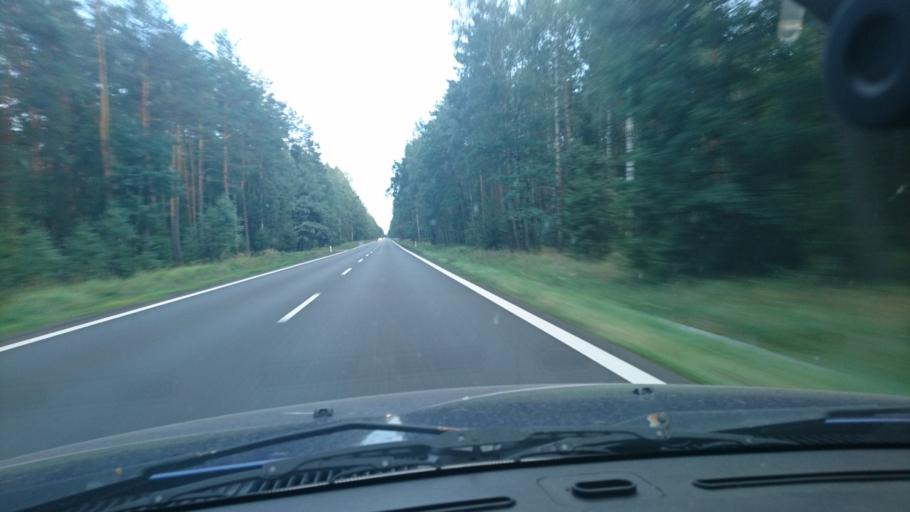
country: PL
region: Silesian Voivodeship
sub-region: Powiat tarnogorski
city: Tworog
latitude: 50.5699
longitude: 18.7110
